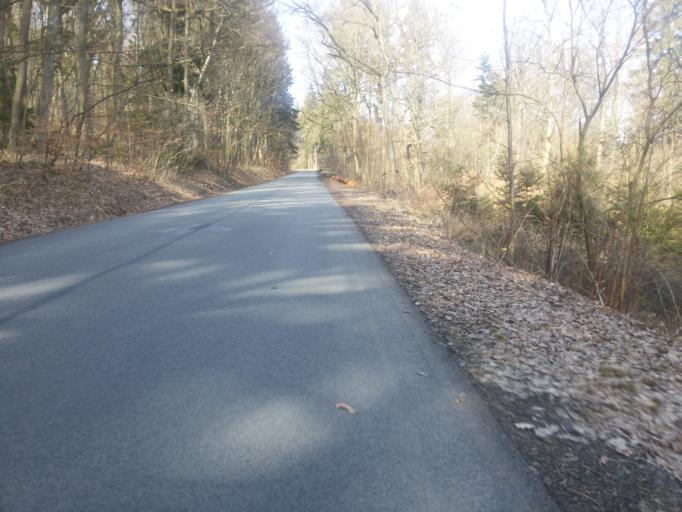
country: CZ
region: South Moravian
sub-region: Okres Brno-Venkov
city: Lomnice
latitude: 49.4204
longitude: 16.4089
